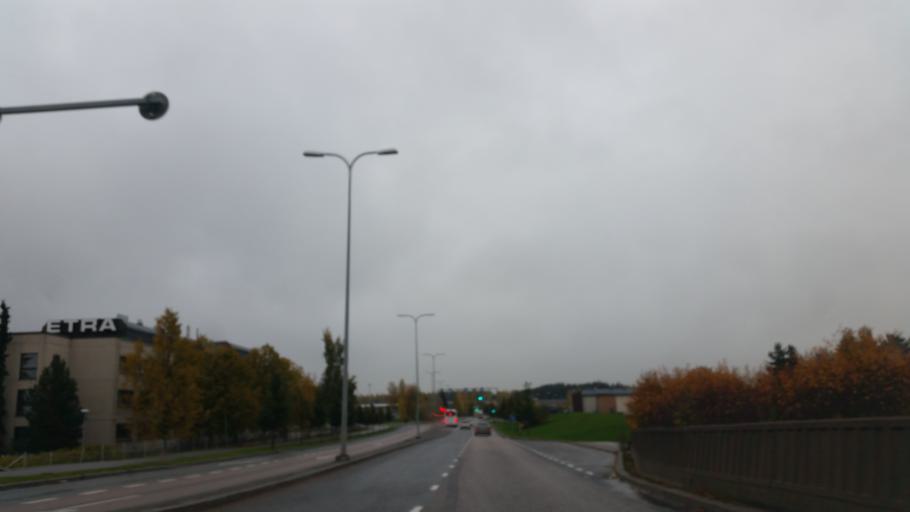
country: FI
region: Uusimaa
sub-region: Helsinki
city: Vantaa
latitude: 60.2841
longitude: 25.0127
